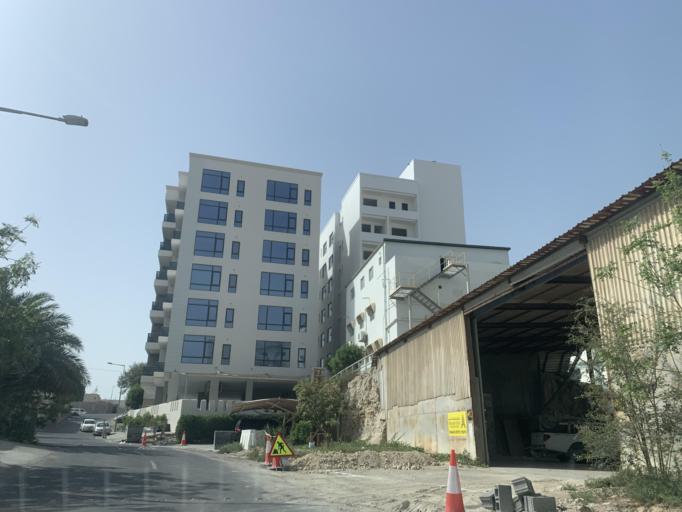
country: BH
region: Northern
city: Ar Rifa'
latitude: 26.1500
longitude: 50.5705
